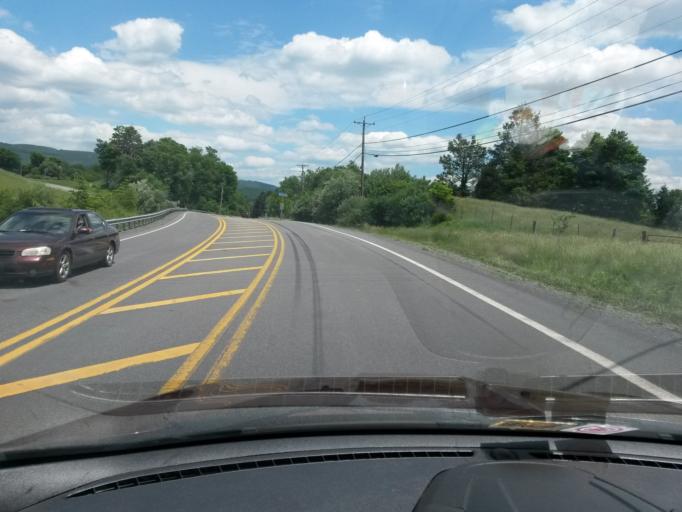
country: US
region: West Virginia
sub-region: Greenbrier County
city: Rainelle
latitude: 37.9529
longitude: -80.6711
